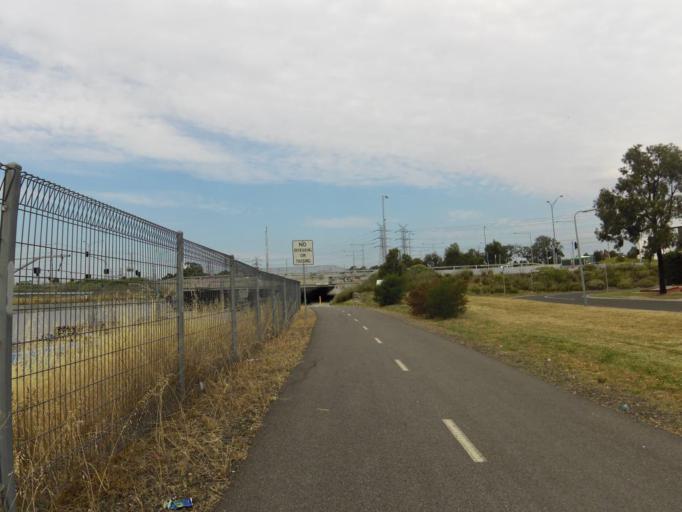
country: AU
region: Victoria
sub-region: Whittlesea
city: Mill Park
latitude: -37.6495
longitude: 145.0651
